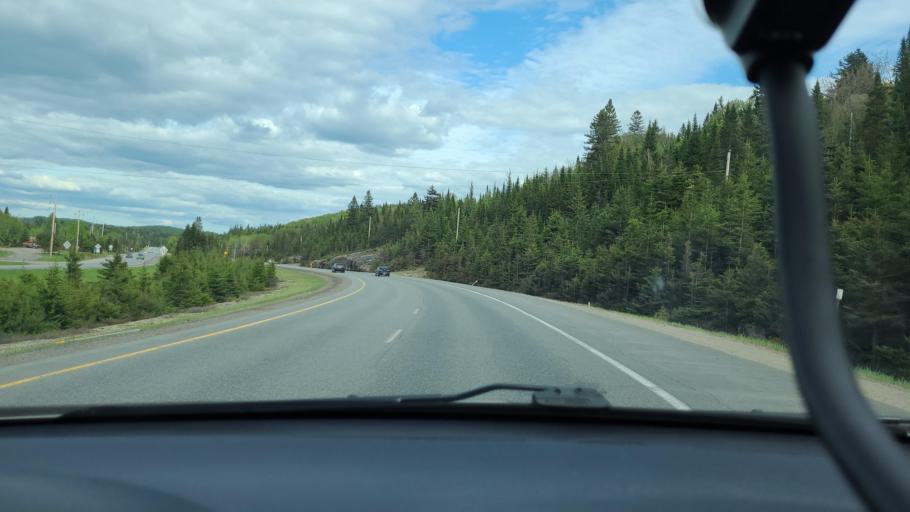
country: CA
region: Quebec
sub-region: Laurentides
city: Sainte-Agathe-des-Monts
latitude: 46.1032
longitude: -74.4128
